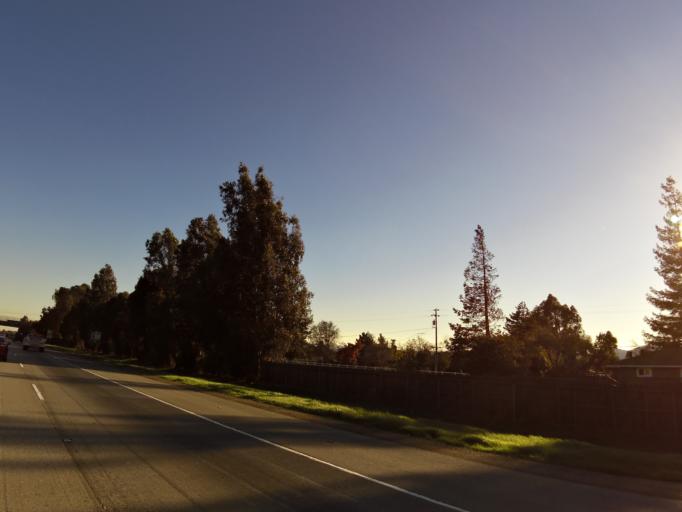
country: US
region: California
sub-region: Santa Clara County
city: Morgan Hill
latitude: 37.1429
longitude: -121.6430
